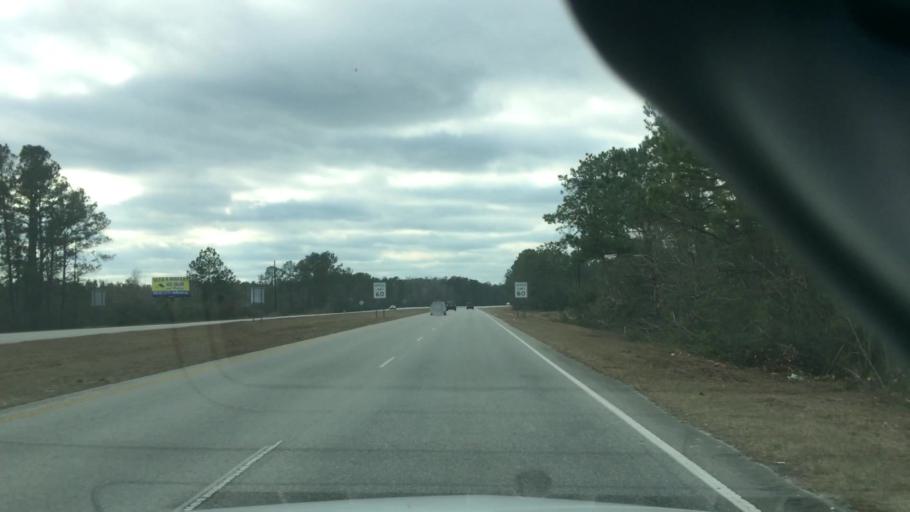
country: US
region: North Carolina
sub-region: Brunswick County
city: Bolivia
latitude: 34.0800
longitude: -78.1403
